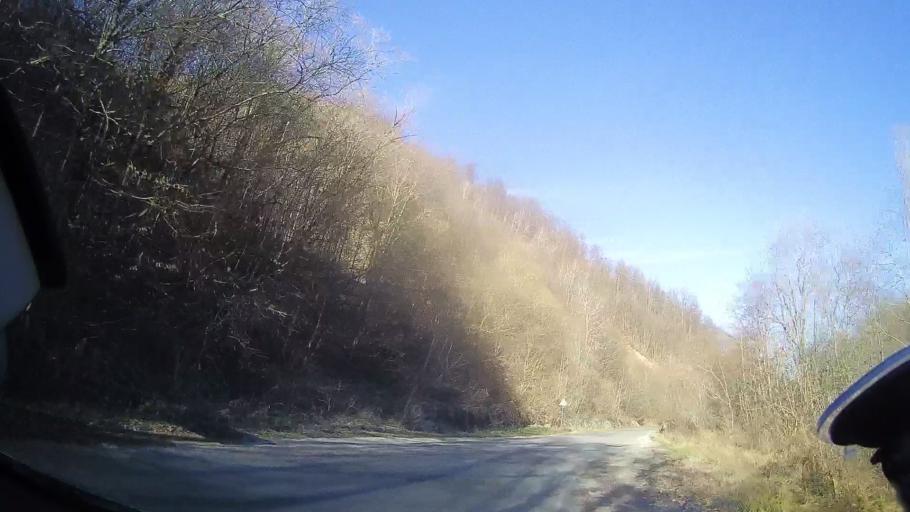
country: RO
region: Cluj
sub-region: Comuna Sacueu
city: Sacuieu
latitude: 46.8433
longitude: 22.8602
